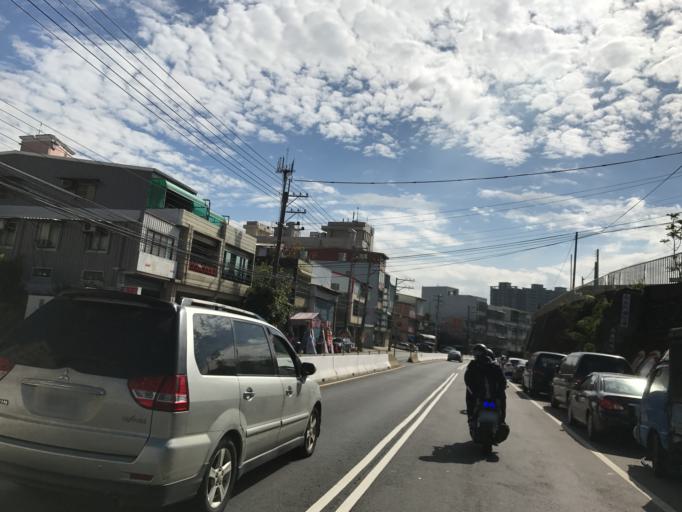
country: TW
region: Taiwan
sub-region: Hsinchu
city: Zhubei
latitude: 24.7628
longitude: 121.0605
